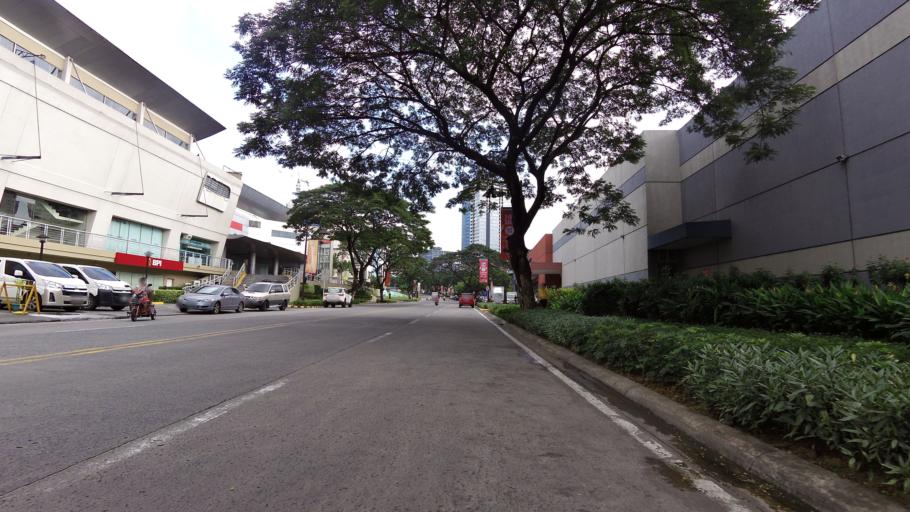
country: PH
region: Metro Manila
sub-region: Pasig
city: Pasig City
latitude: 14.5844
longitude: 121.0763
